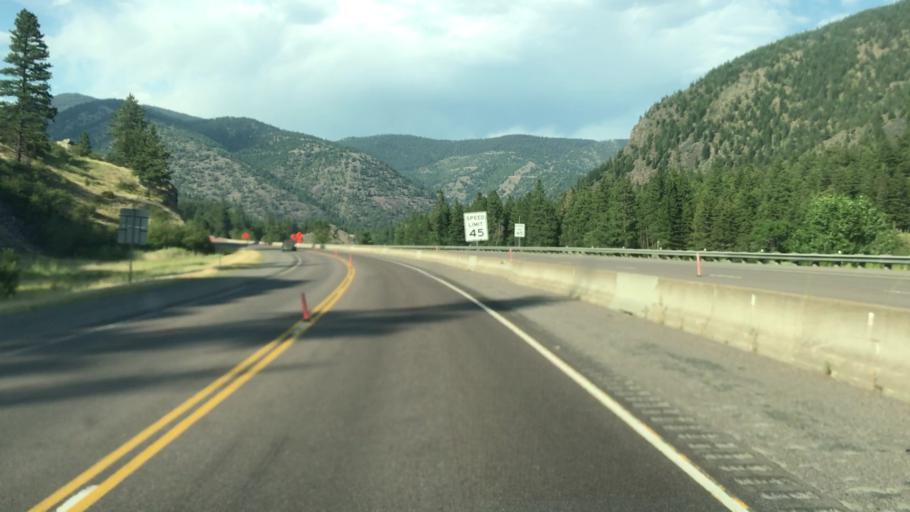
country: US
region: Montana
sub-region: Missoula County
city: Frenchtown
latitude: 47.0053
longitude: -114.5521
